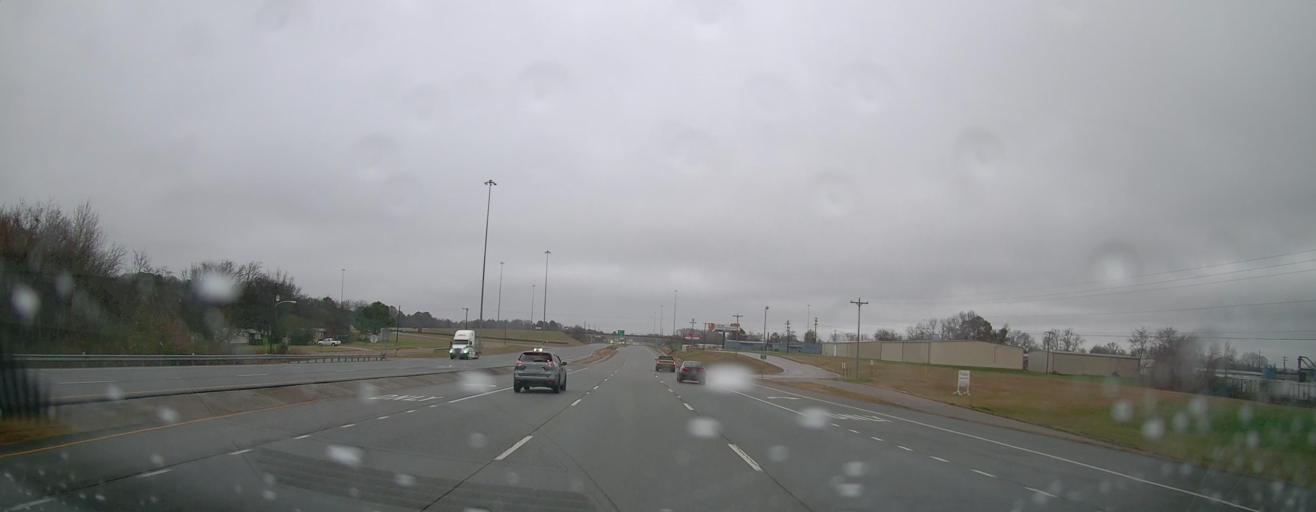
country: US
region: Alabama
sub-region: Morgan County
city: Decatur
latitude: 34.6073
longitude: -87.0313
